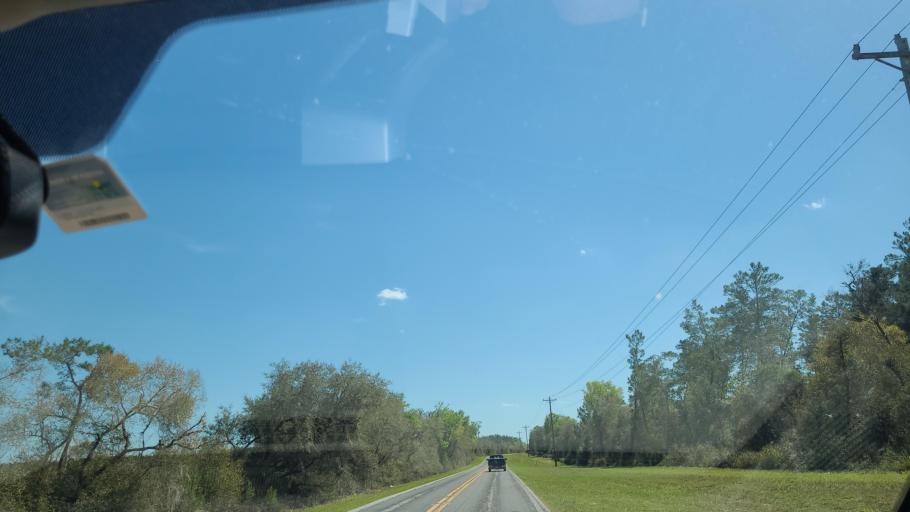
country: US
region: Florida
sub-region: Marion County
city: Citra
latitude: 29.3923
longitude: -81.8897
